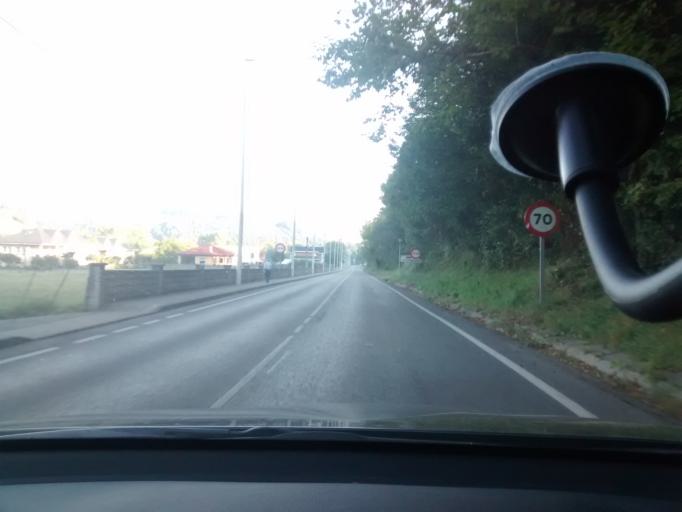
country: ES
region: Cantabria
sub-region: Provincia de Cantabria
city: Entrambasaguas
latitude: 43.3548
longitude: -3.7085
